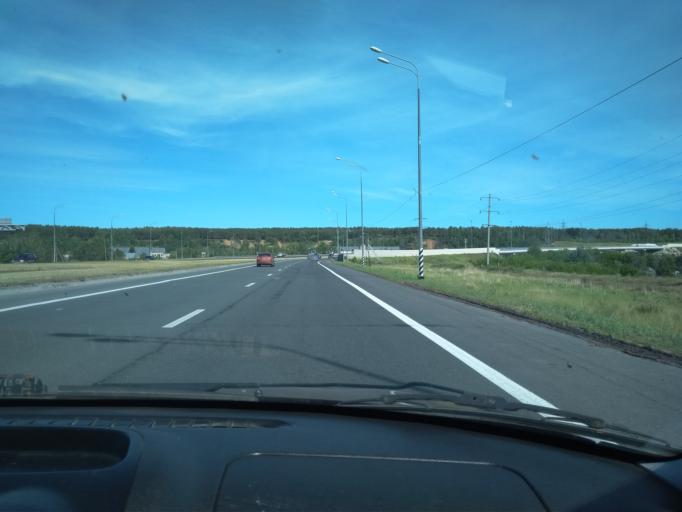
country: RU
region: Ulyanovsk
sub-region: Ulyanovskiy Rayon
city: Ulyanovsk
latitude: 54.3566
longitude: 48.5025
